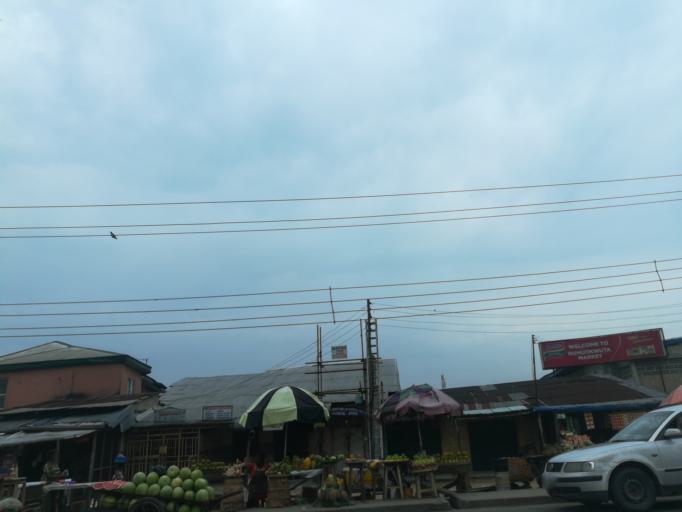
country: NG
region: Rivers
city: Port Harcourt
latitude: 4.8401
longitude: 6.9863
